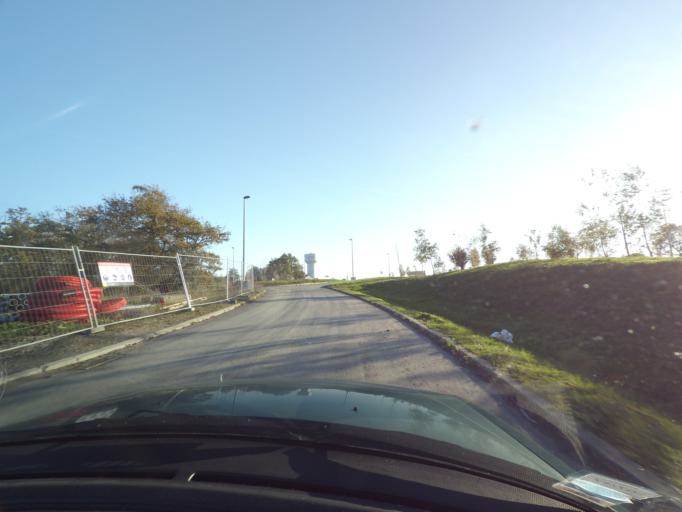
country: FR
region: Pays de la Loire
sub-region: Departement de la Loire-Atlantique
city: Le Bignon
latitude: 47.0979
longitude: -1.4494
